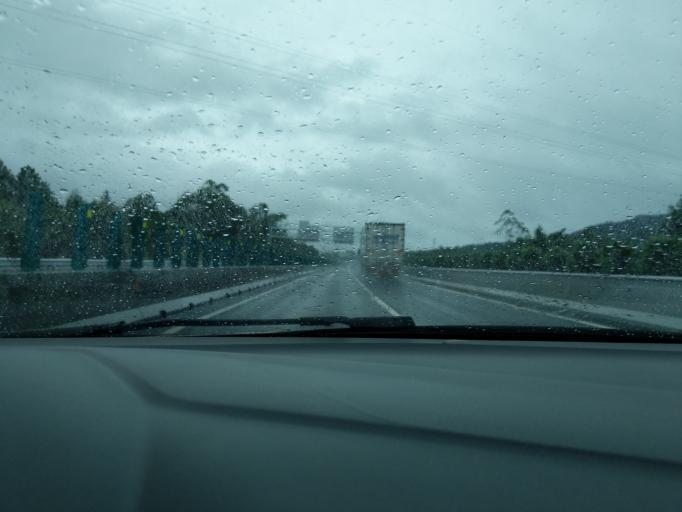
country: CN
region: Guangdong
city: Pingshi
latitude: 22.2507
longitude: 112.3070
